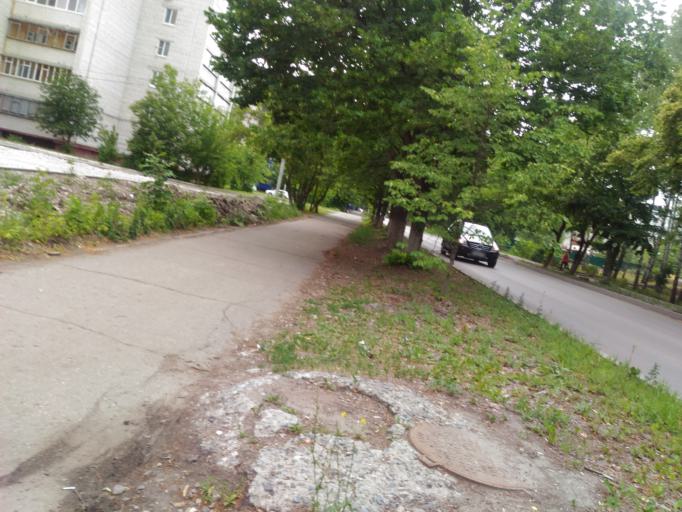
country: RU
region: Ulyanovsk
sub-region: Ulyanovskiy Rayon
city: Ulyanovsk
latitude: 54.2818
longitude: 48.2919
